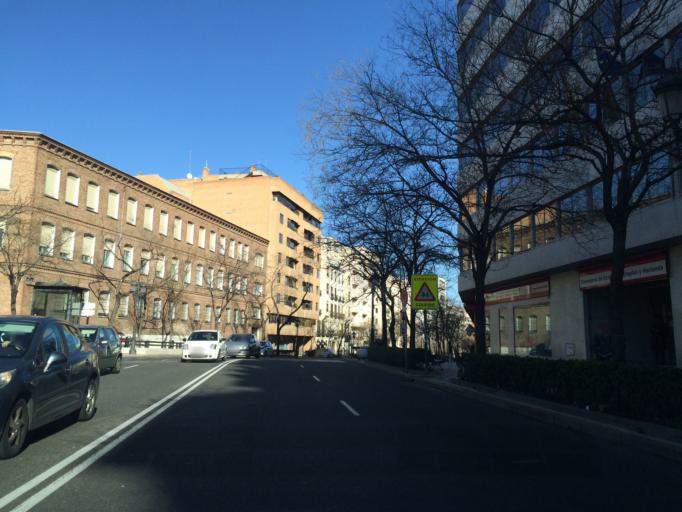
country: ES
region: Madrid
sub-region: Provincia de Madrid
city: Chamberi
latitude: 40.4325
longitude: -3.6970
